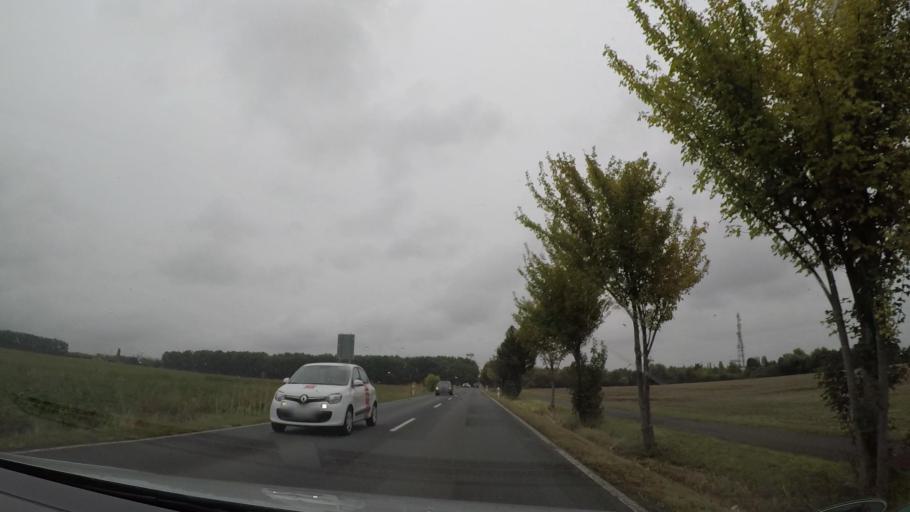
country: DE
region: Saxony-Anhalt
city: Ebendorf
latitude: 52.1710
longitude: 11.5977
